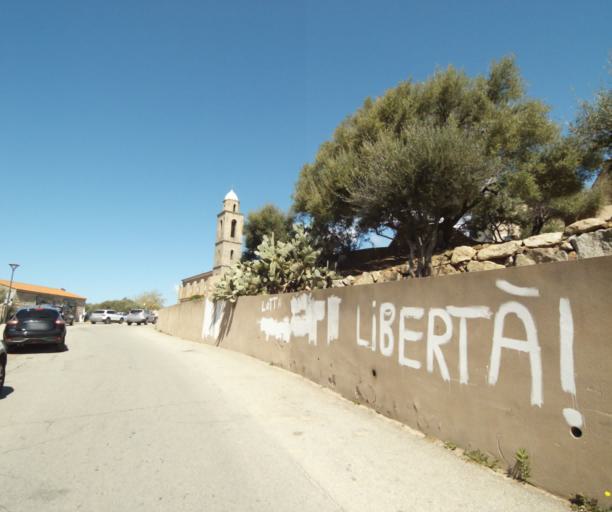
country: FR
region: Corsica
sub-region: Departement de la Corse-du-Sud
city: Propriano
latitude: 41.6747
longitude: 8.9056
